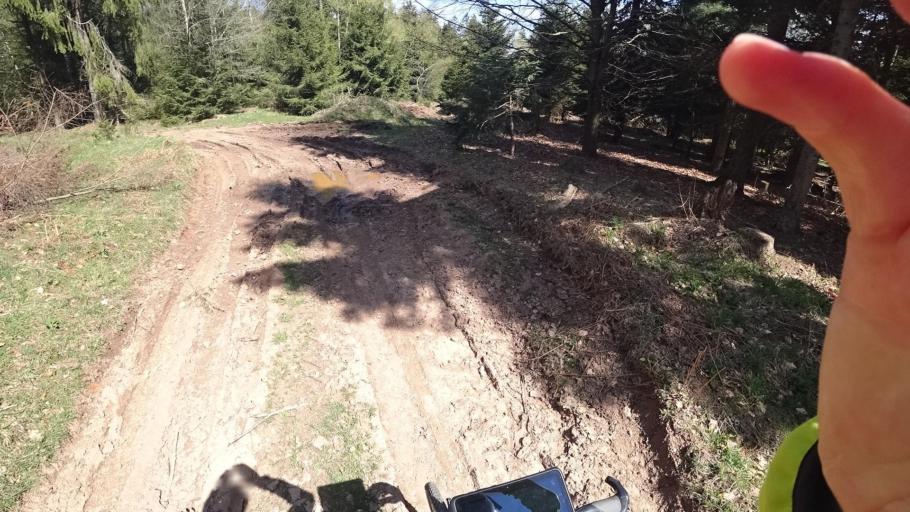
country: DE
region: Rheinland-Pfalz
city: Gusenburg
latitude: 49.6522
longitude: 6.9148
